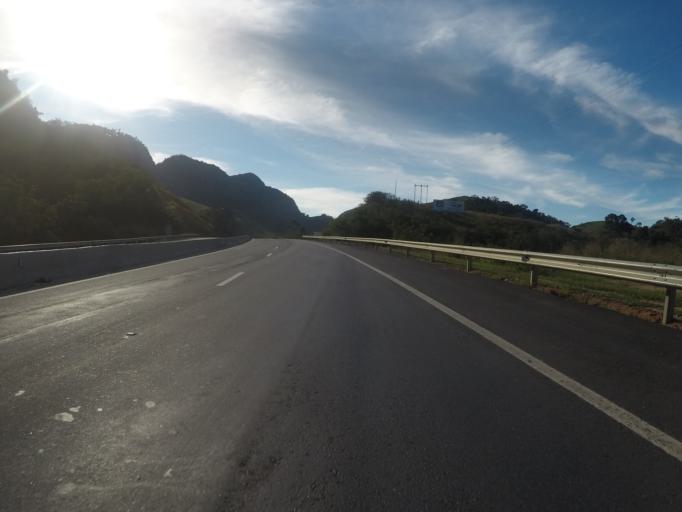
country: BR
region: Espirito Santo
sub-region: Ibiracu
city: Ibiracu
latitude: -19.8492
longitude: -40.3833
